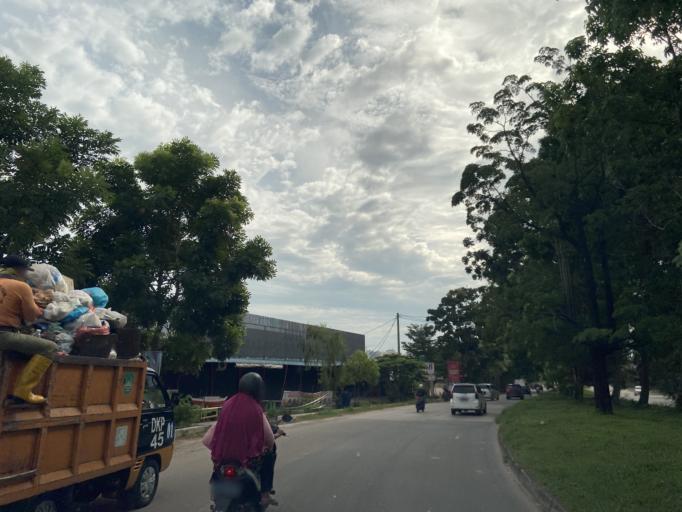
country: SG
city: Singapore
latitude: 1.1399
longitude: 104.0006
